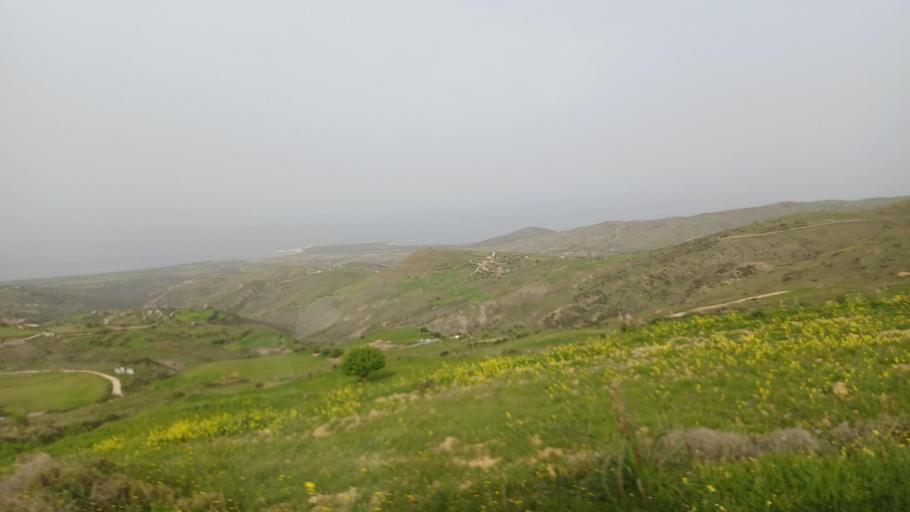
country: CY
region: Pafos
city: Pegeia
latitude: 34.9523
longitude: 32.3786
